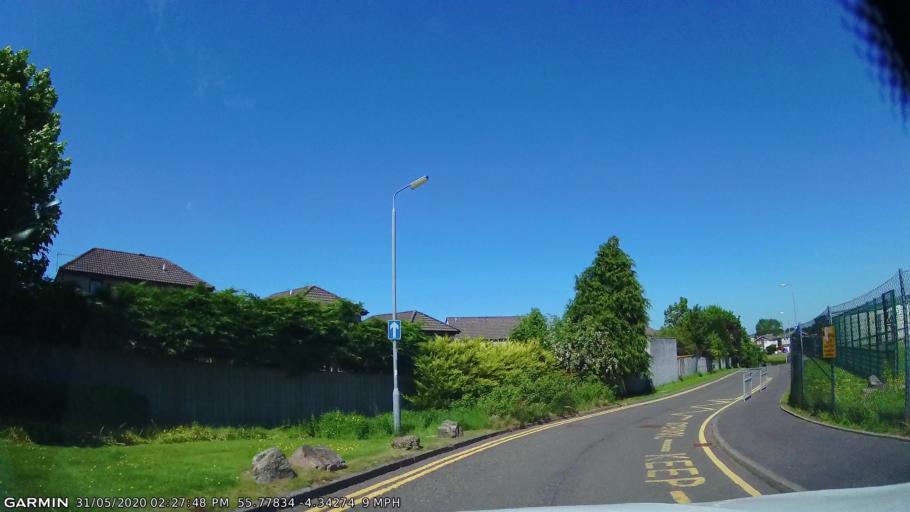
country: GB
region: Scotland
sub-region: East Renfrewshire
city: Newton Mearns
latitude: 55.7783
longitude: -4.3428
